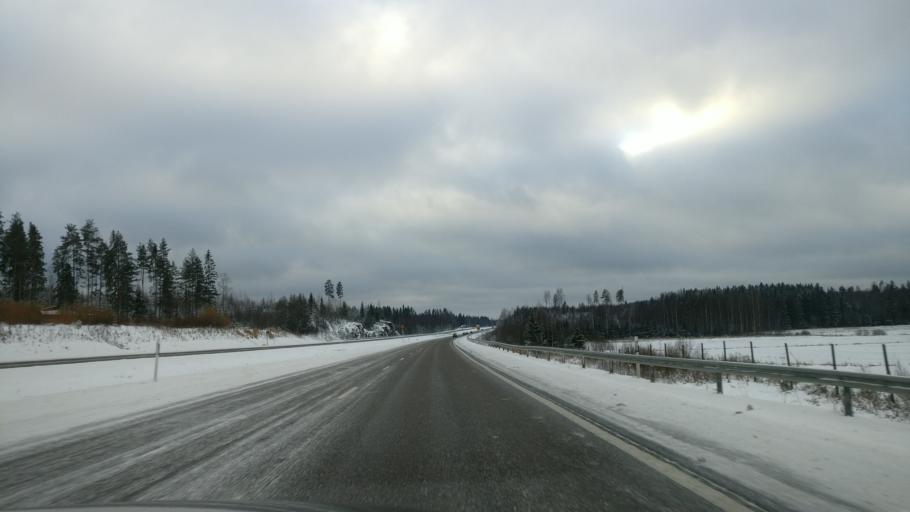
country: FI
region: Paijanne Tavastia
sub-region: Lahti
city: Nastola
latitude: 61.0751
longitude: 25.8864
